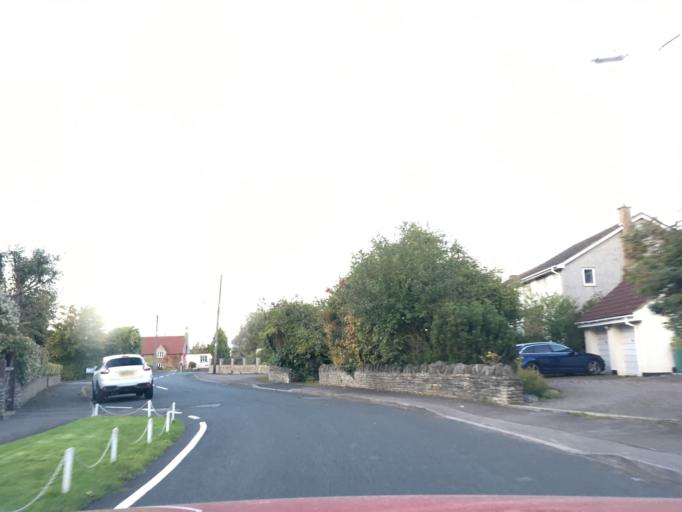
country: GB
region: England
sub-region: South Gloucestershire
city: Stoke Gifford
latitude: 51.5201
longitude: -2.5384
